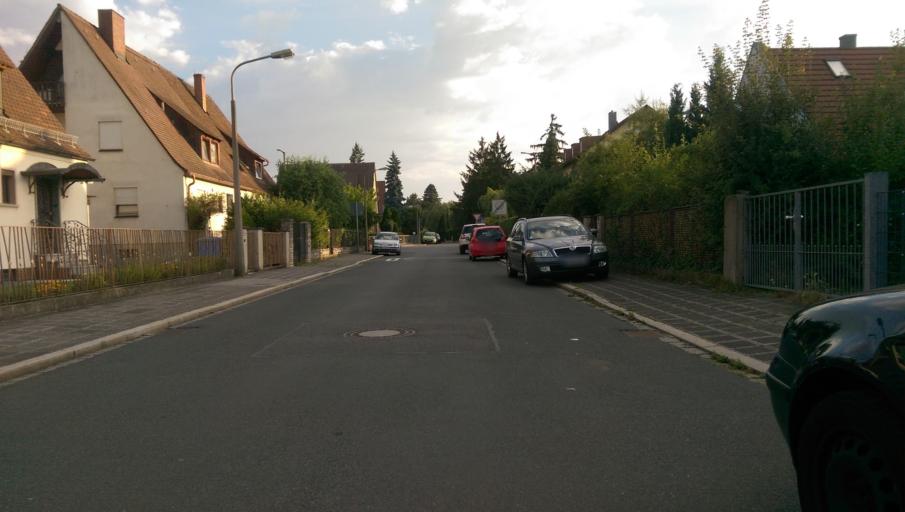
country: DE
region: Bavaria
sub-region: Regierungsbezirk Mittelfranken
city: Wetzendorf
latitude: 49.4782
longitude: 11.0560
